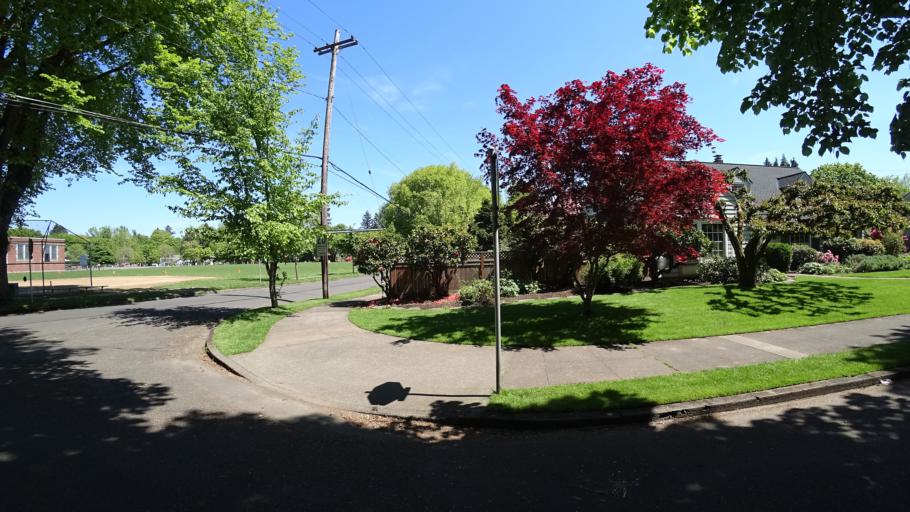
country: US
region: Oregon
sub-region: Clackamas County
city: Milwaukie
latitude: 45.4674
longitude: -122.6293
